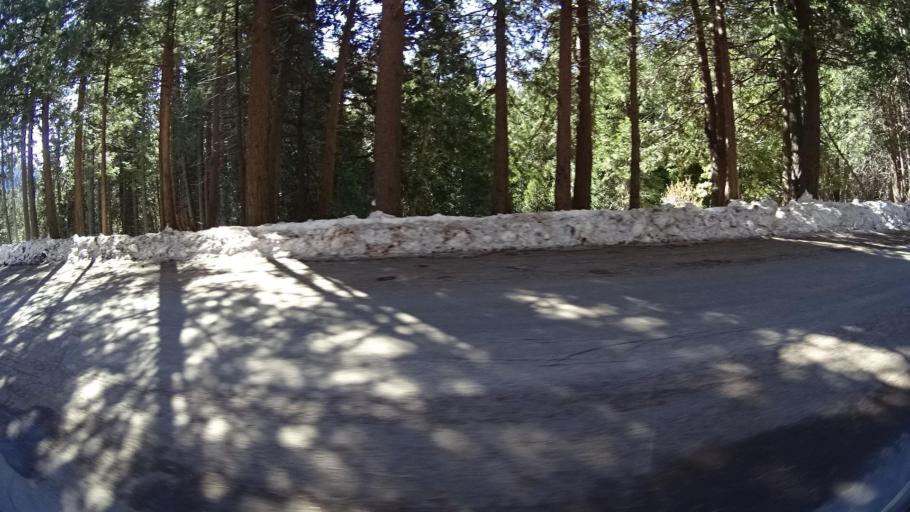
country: US
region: California
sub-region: Kern County
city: Alta Sierra
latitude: 35.7143
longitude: -118.5571
